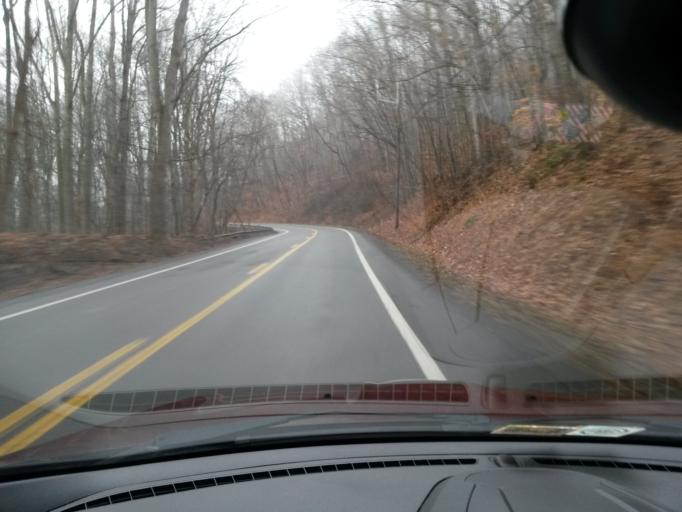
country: US
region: West Virginia
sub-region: Greenbrier County
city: Lewisburg
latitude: 37.8727
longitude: -80.5341
